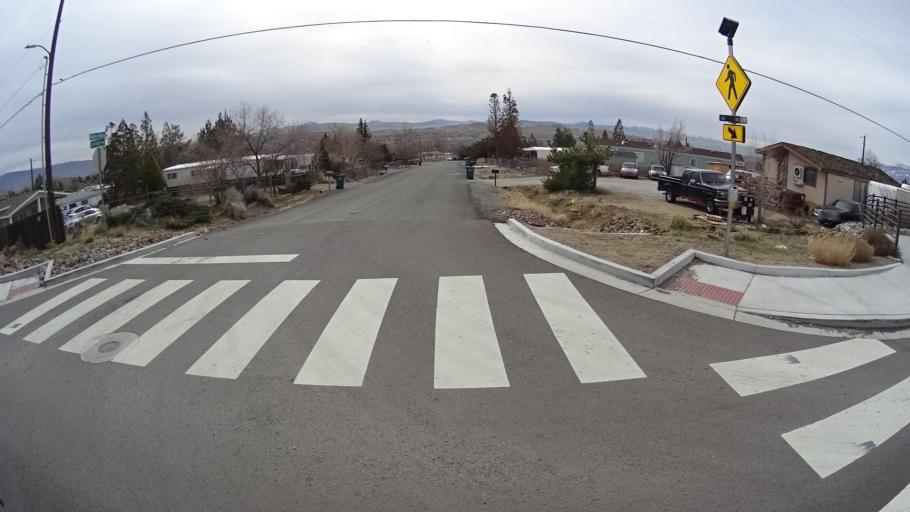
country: US
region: Nevada
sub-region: Washoe County
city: Sun Valley
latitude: 39.6093
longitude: -119.7787
